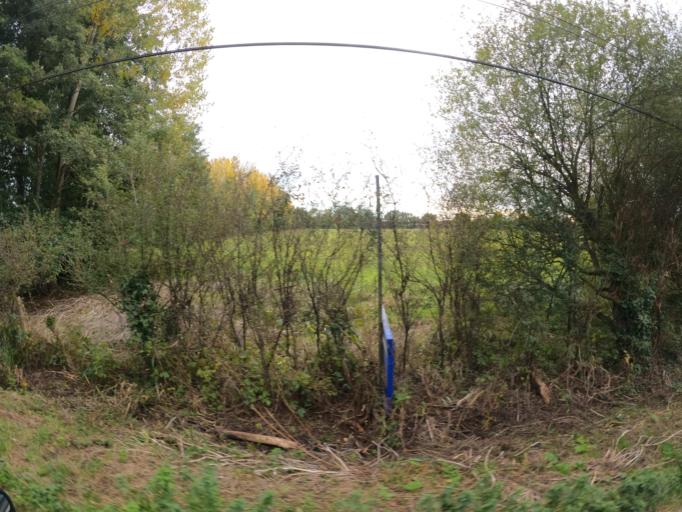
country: FR
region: Pays de la Loire
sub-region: Departement de Maine-et-Loire
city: Saint-Christophe-du-Bois
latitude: 47.0262
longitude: -0.9506
